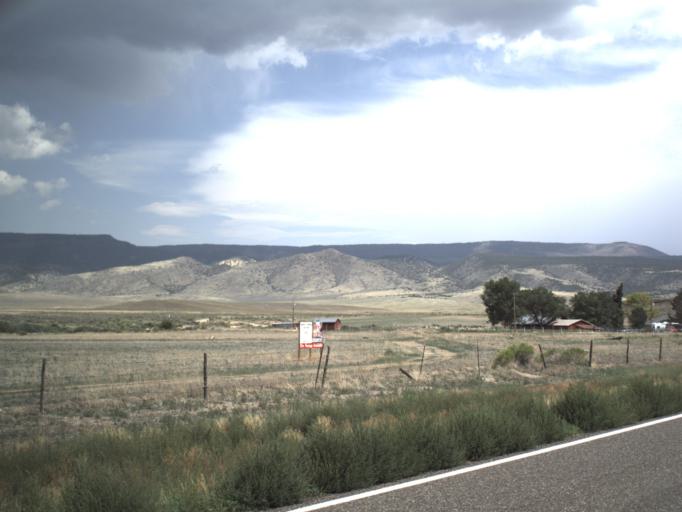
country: US
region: Utah
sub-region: Piute County
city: Junction
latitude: 38.1618
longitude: -112.0107
